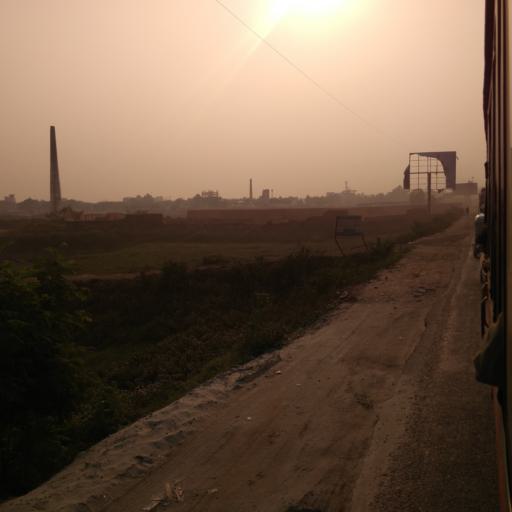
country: BD
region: Dhaka
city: Tungi
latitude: 23.8960
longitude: 90.3398
